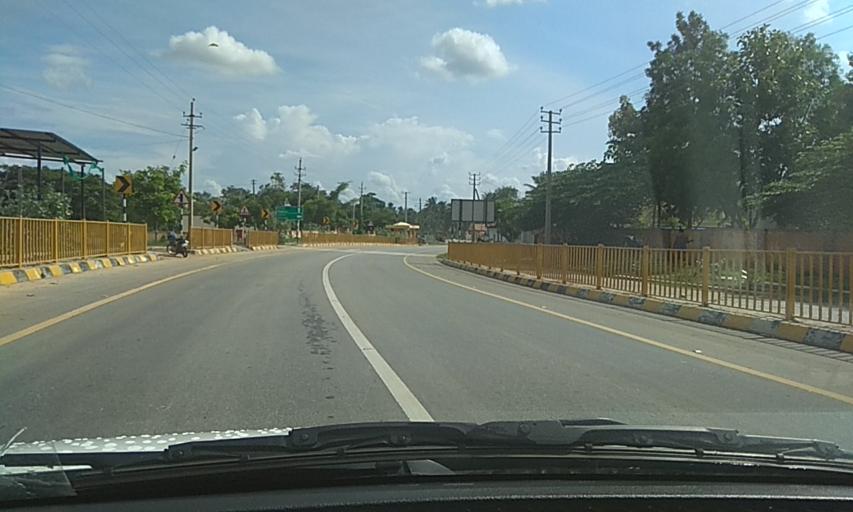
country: IN
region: Karnataka
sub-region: Mandya
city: Maddur
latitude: 12.6650
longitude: 77.0539
